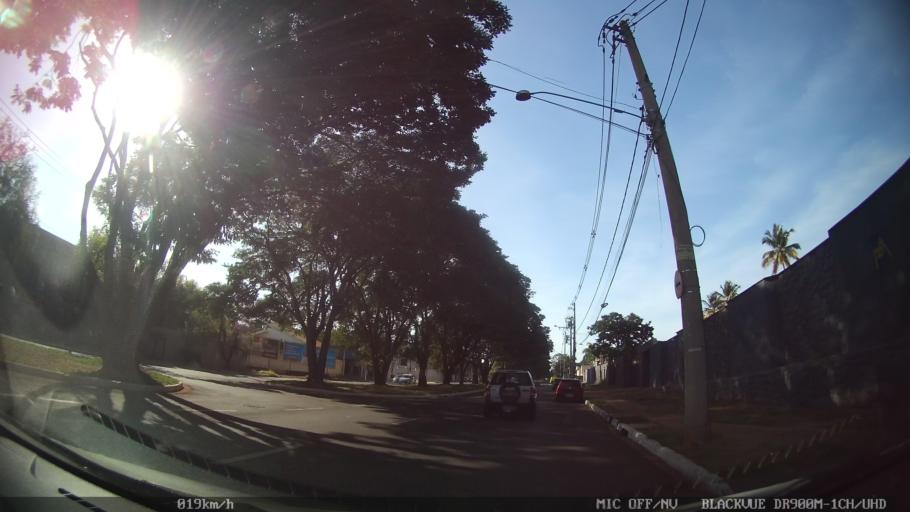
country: BR
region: Sao Paulo
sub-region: Ribeirao Preto
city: Ribeirao Preto
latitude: -21.2185
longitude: -47.8149
